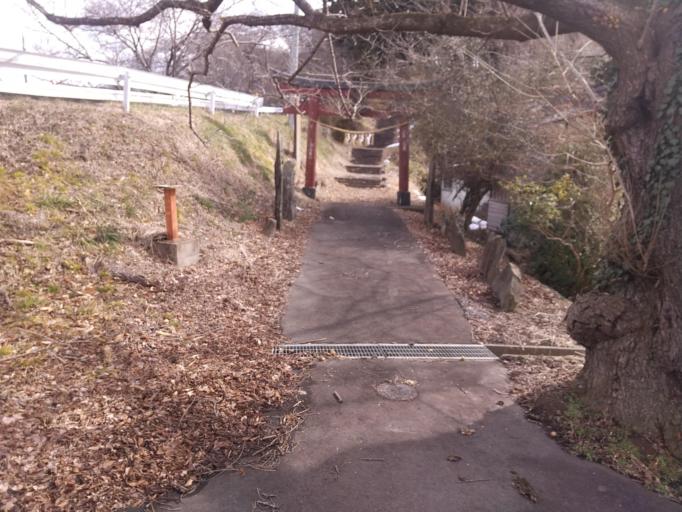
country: JP
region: Miyagi
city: Wakuya
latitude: 38.7042
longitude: 141.2783
